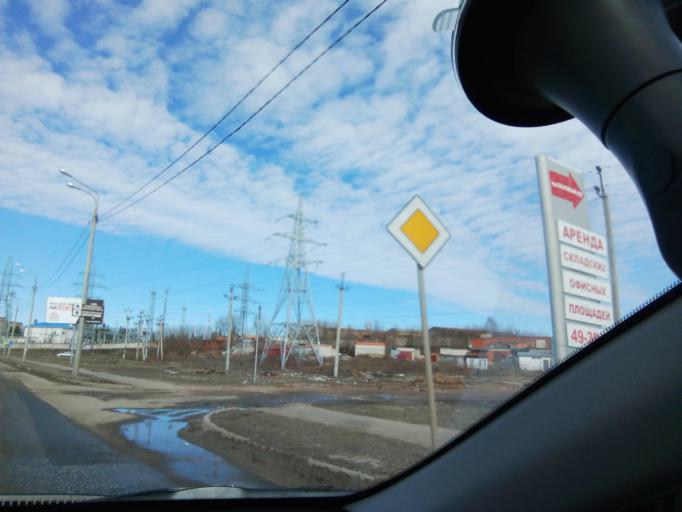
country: RU
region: Chuvashia
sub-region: Cheboksarskiy Rayon
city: Cheboksary
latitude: 56.1085
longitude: 47.2458
